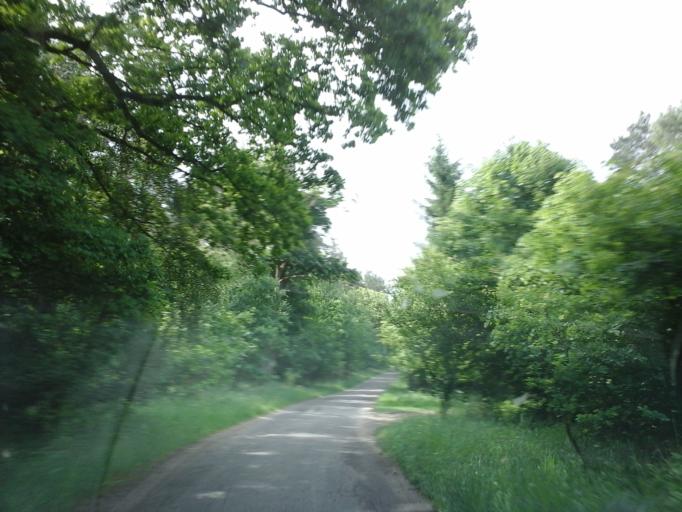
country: PL
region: West Pomeranian Voivodeship
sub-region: Powiat choszczenski
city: Drawno
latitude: 53.1990
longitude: 15.7574
